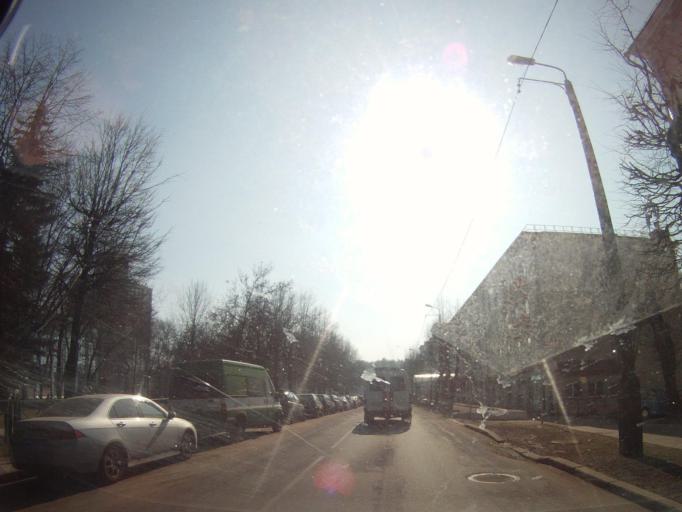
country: BY
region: Minsk
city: Minsk
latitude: 53.9263
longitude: 27.6129
